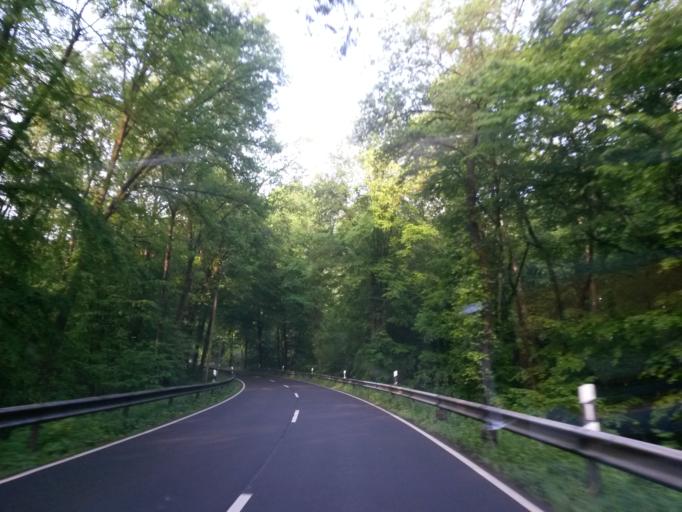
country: DE
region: North Rhine-Westphalia
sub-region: Regierungsbezirk Koln
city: Much
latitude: 50.8814
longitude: 7.3611
